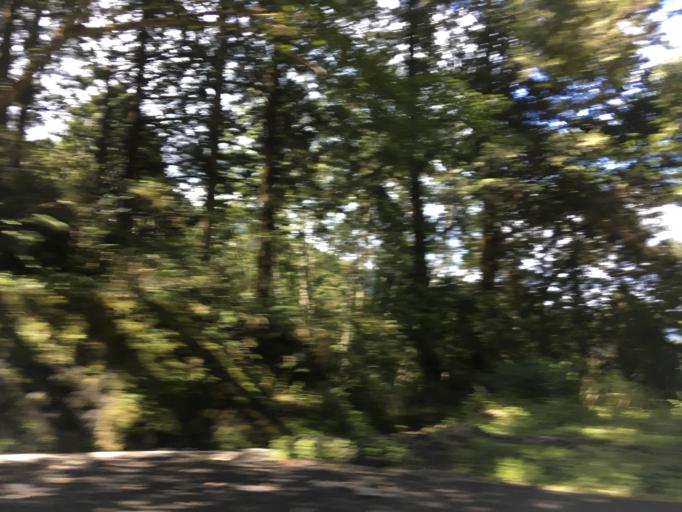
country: TW
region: Taiwan
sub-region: Yilan
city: Yilan
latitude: 24.5045
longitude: 121.5249
